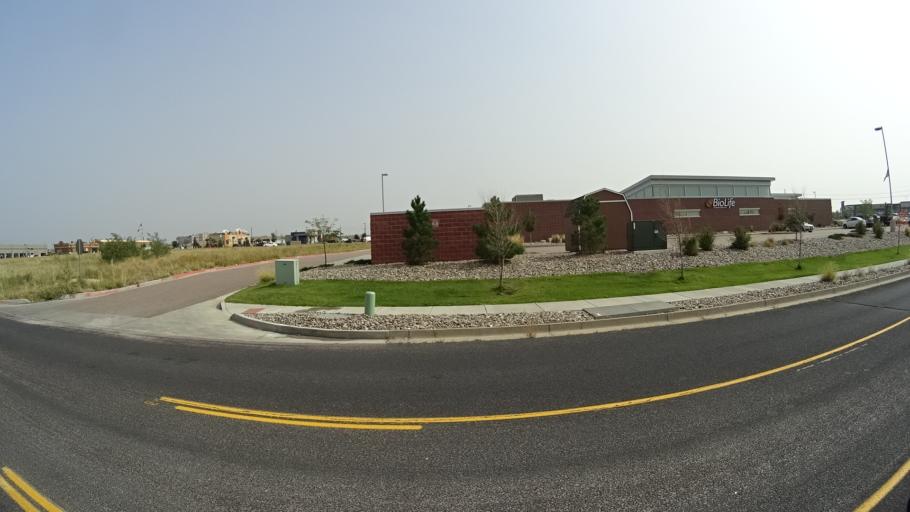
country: US
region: Colorado
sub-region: El Paso County
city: Cimarron Hills
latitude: 38.9243
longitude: -104.7222
